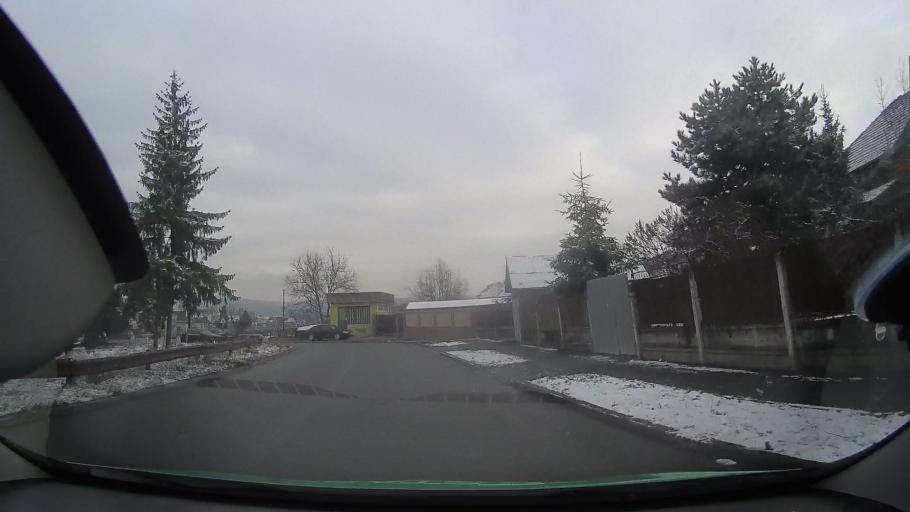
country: RO
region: Mures
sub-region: Comuna Ludus
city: Ludus
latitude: 46.4683
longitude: 24.0924
